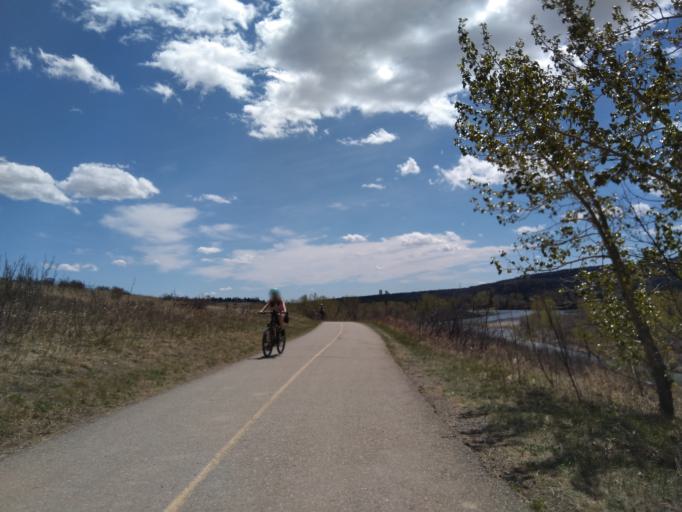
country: CA
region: Alberta
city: Calgary
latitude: 51.0947
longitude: -114.1845
